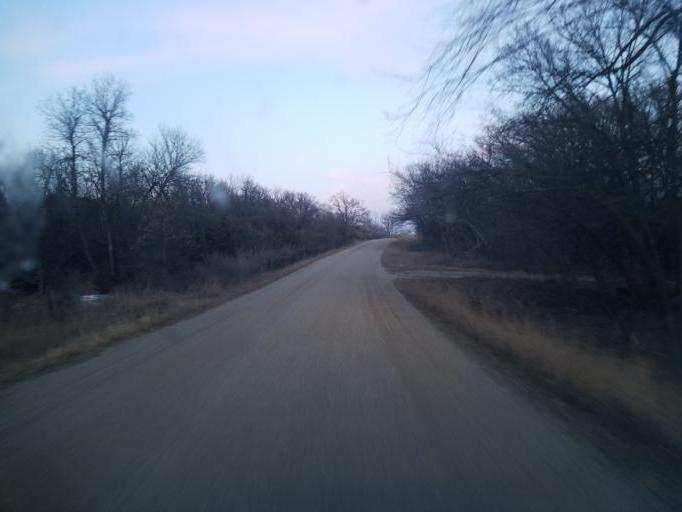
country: US
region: Nebraska
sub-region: Knox County
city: Center
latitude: 42.6117
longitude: -97.8587
